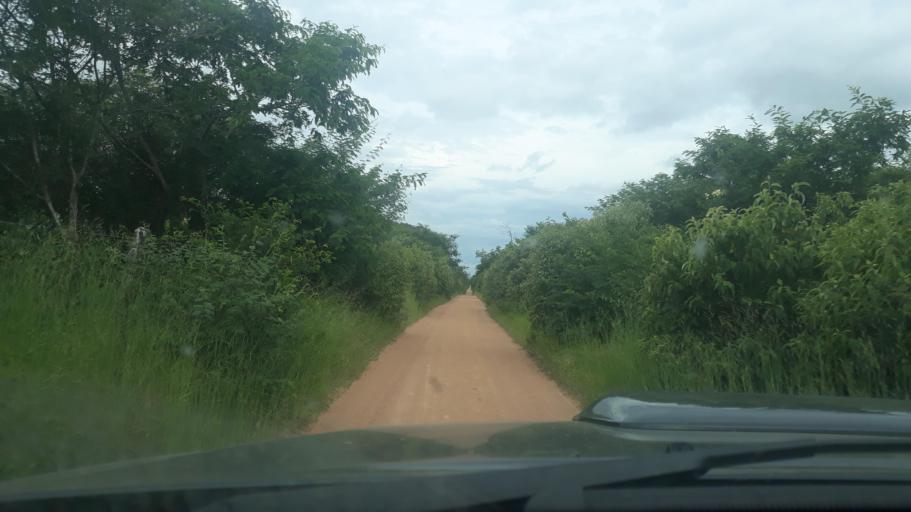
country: BR
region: Bahia
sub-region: Riacho De Santana
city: Riacho de Santana
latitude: -13.8573
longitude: -43.0434
